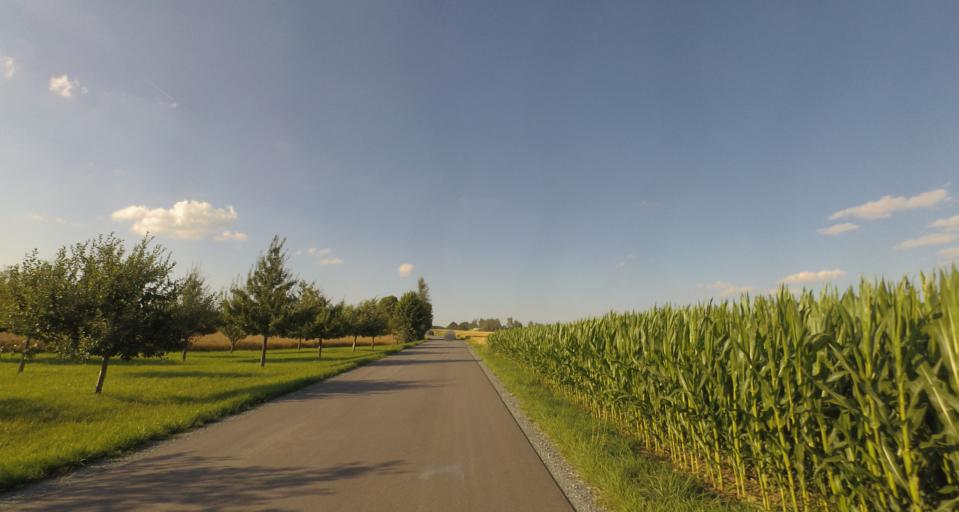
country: DE
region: Bavaria
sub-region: Upper Bavaria
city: Chieming
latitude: 47.9079
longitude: 12.5250
